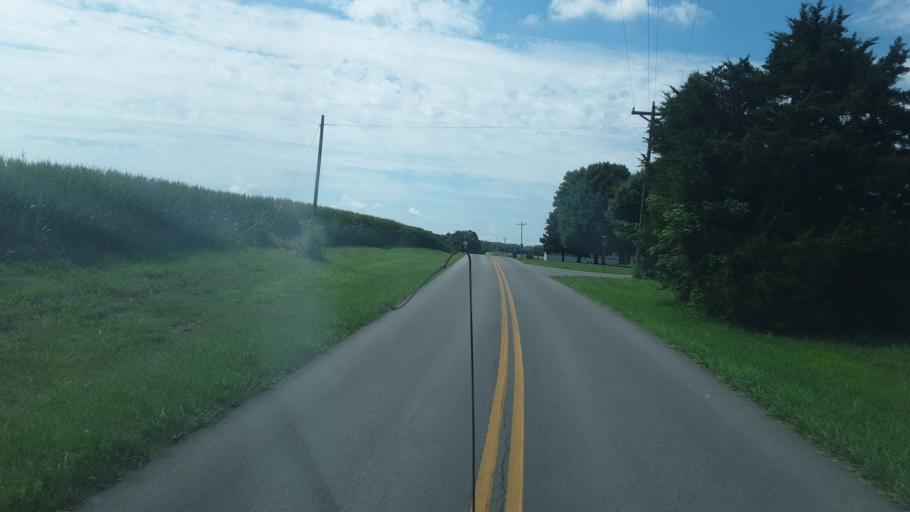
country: US
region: Kentucky
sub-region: Christian County
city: Oak Grove
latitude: 36.7423
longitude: -87.3213
